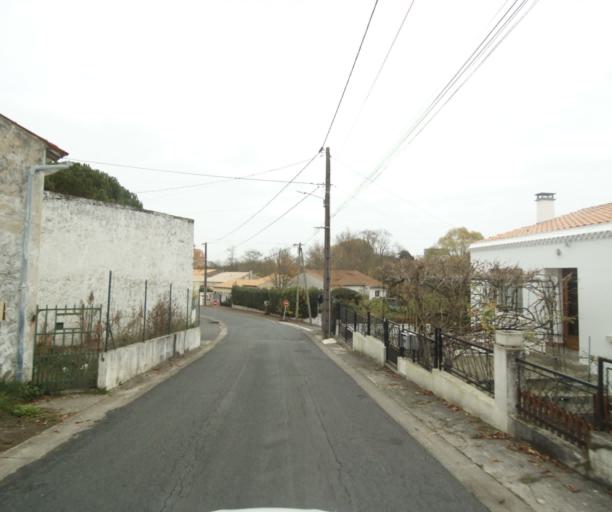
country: FR
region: Poitou-Charentes
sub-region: Departement de la Charente-Maritime
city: Saintes
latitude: 45.7291
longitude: -0.6406
